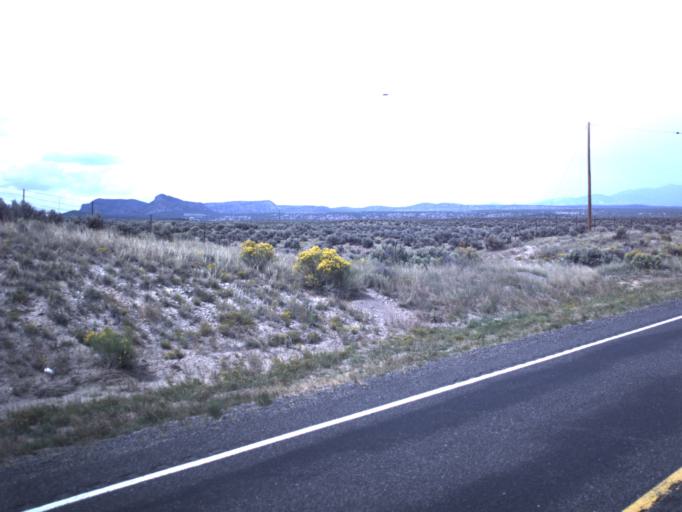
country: US
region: Utah
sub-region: Garfield County
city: Panguitch
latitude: 37.9371
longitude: -112.4252
